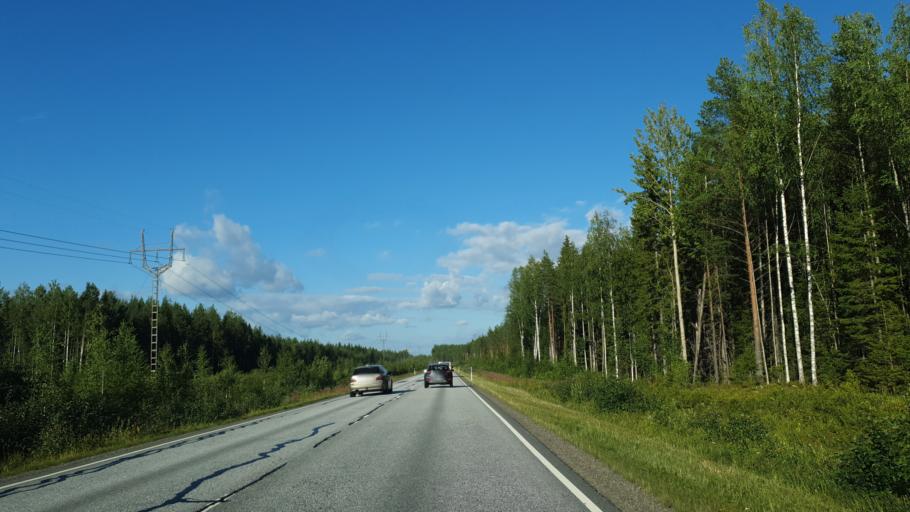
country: FI
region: North Karelia
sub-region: Joensuu
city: Outokumpu
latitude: 62.5333
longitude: 29.0983
